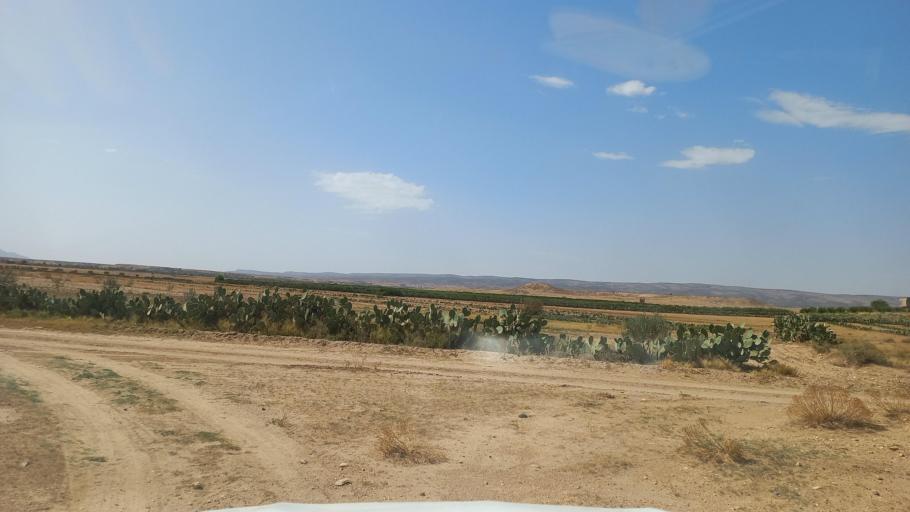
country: TN
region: Al Qasrayn
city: Kasserine
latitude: 35.2590
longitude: 8.9719
